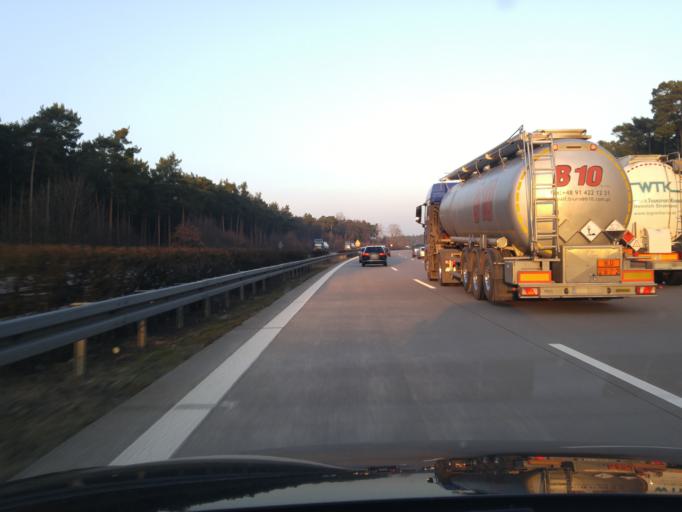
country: DE
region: Brandenburg
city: Wollin
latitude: 52.3353
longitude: 12.5059
